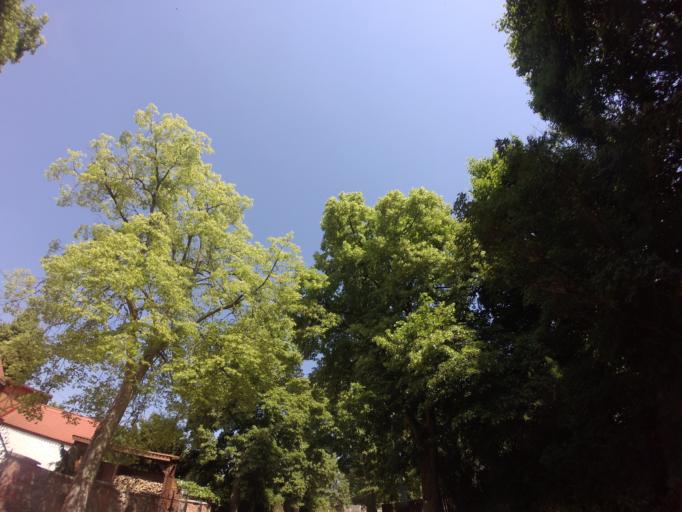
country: PL
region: West Pomeranian Voivodeship
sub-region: Powiat choszczenski
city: Drawno
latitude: 53.1320
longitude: 15.8462
